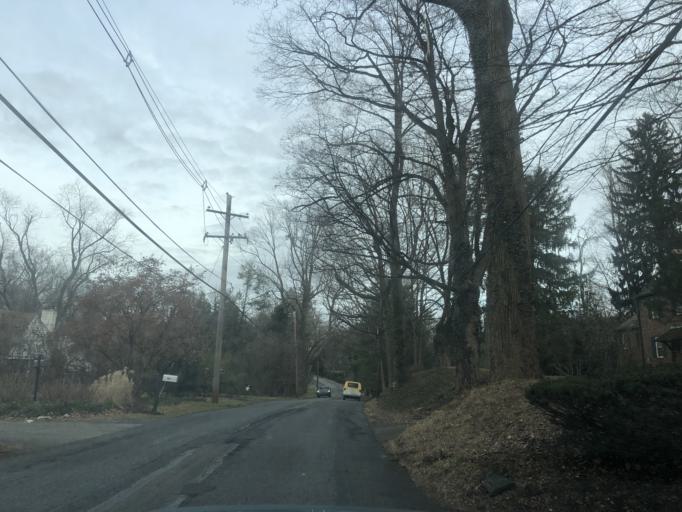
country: US
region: Pennsylvania
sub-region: Delaware County
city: Radnor
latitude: 40.0366
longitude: -75.3333
